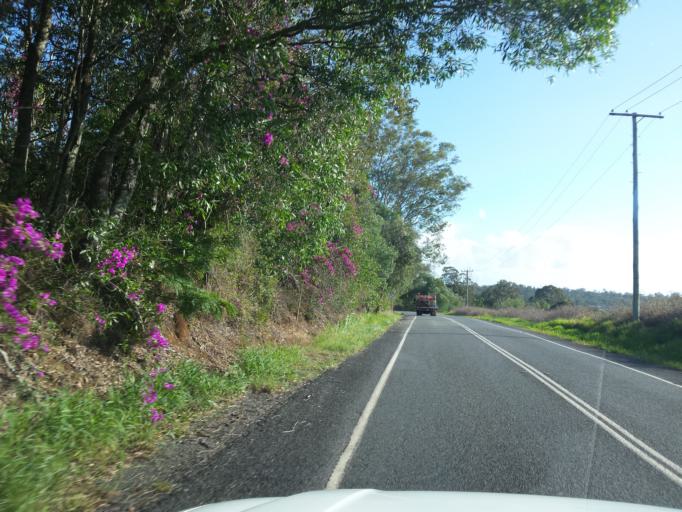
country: AU
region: Queensland
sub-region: Logan
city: Windaroo
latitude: -27.7715
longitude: 153.1901
